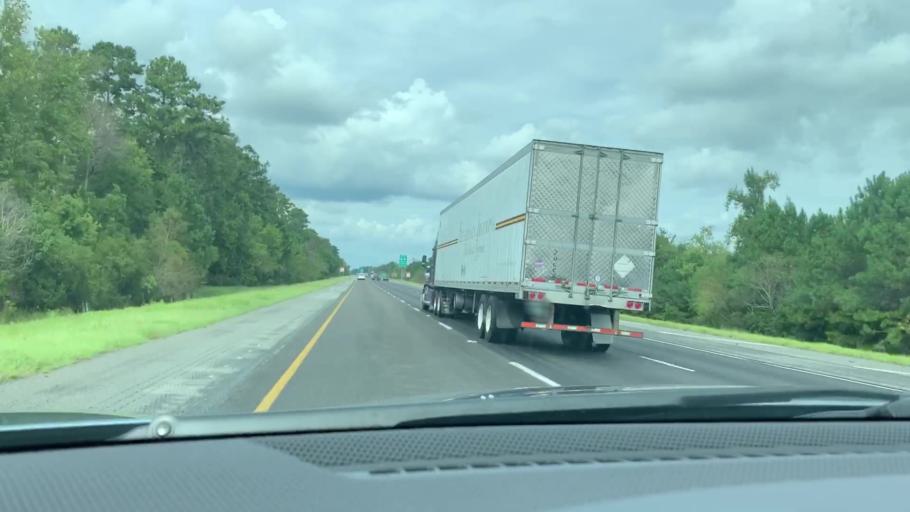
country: US
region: Georgia
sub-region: Liberty County
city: Midway
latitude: 31.7564
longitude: -81.3825
